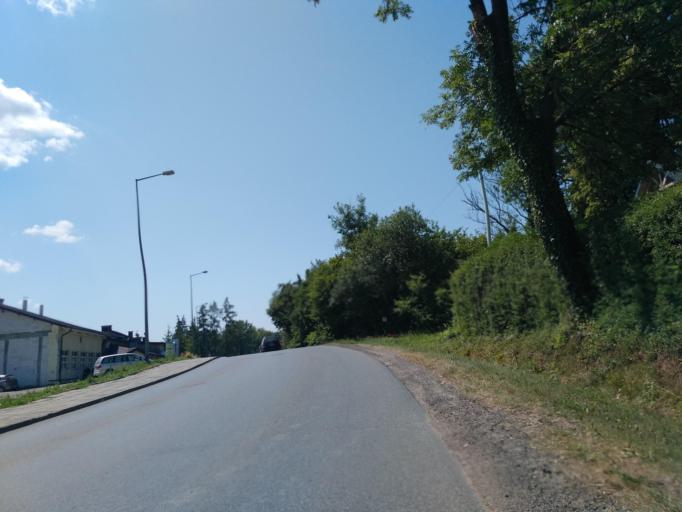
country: PL
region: Subcarpathian Voivodeship
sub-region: Powiat sanocki
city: Sanok
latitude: 49.5677
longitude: 22.1574
